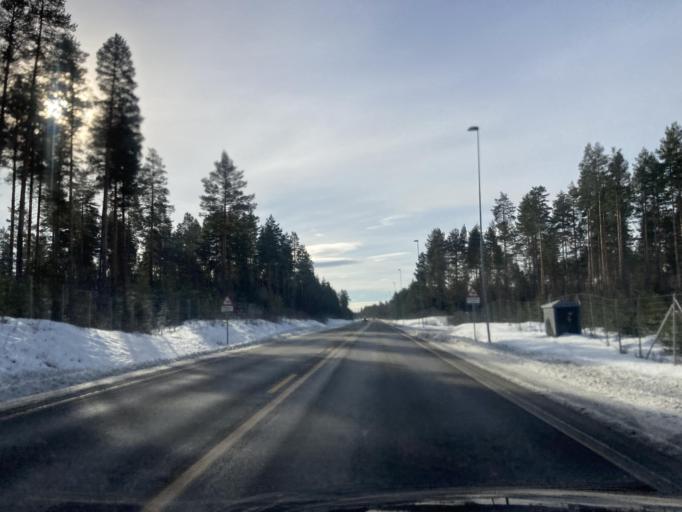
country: NO
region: Hedmark
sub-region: Loten
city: Loten
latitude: 60.7560
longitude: 11.3044
